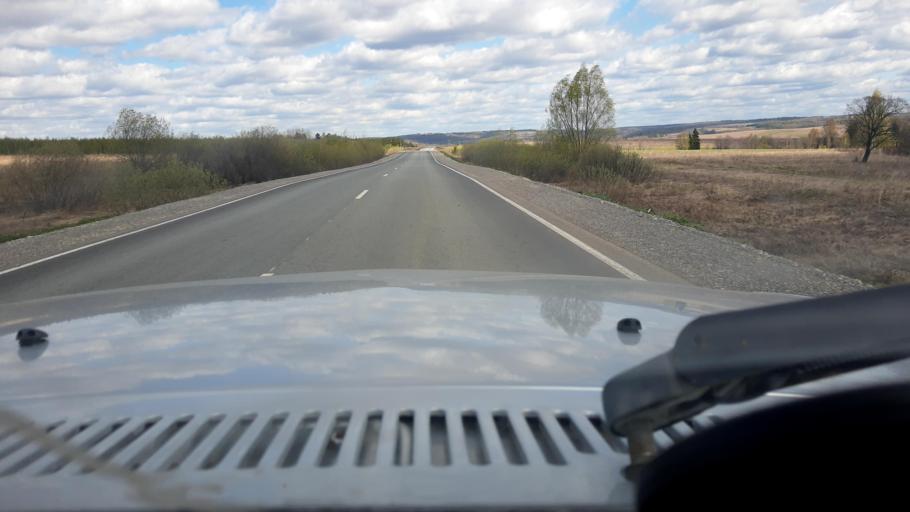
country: RU
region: Bashkortostan
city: Pavlovka
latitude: 55.3262
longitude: 56.3552
